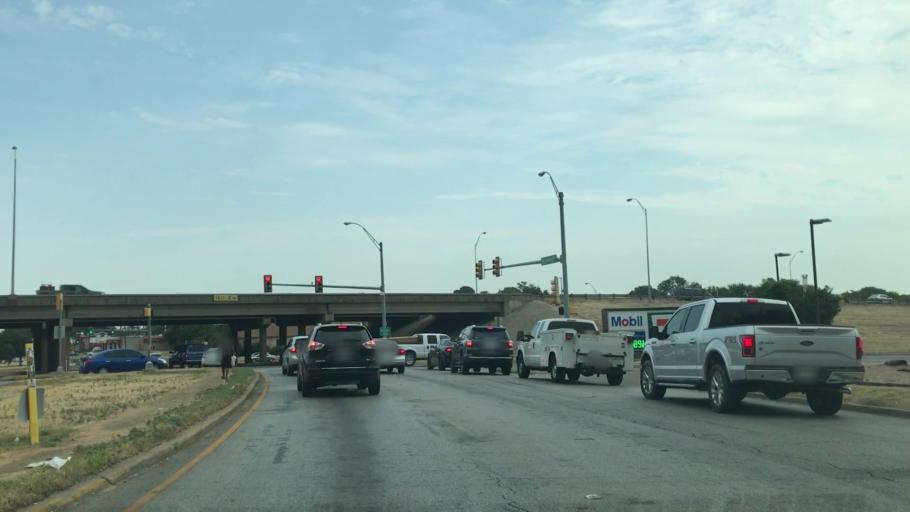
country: US
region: Texas
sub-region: Tarrant County
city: Haltom City
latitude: 32.7742
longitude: -97.2874
